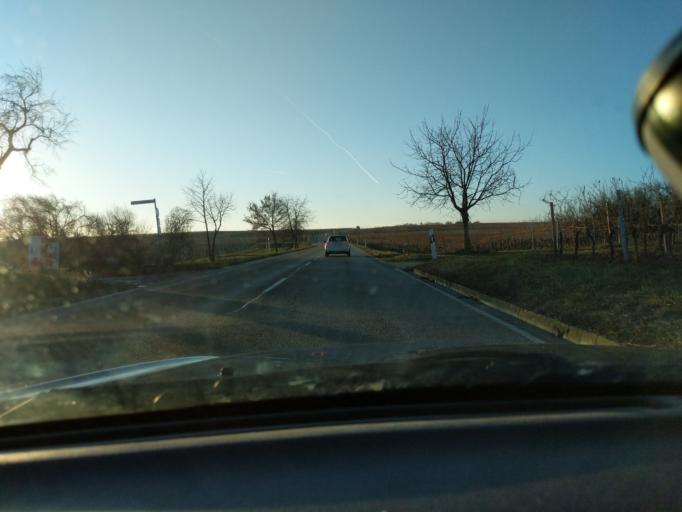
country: DE
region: Rheinland-Pfalz
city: Dackenheim
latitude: 49.5215
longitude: 8.1783
